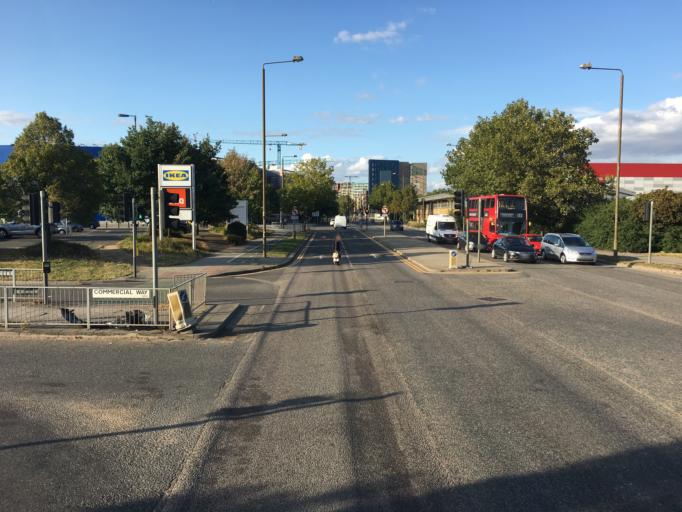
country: GB
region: England
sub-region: Greater London
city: Blackheath
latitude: 51.4882
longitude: 0.0172
